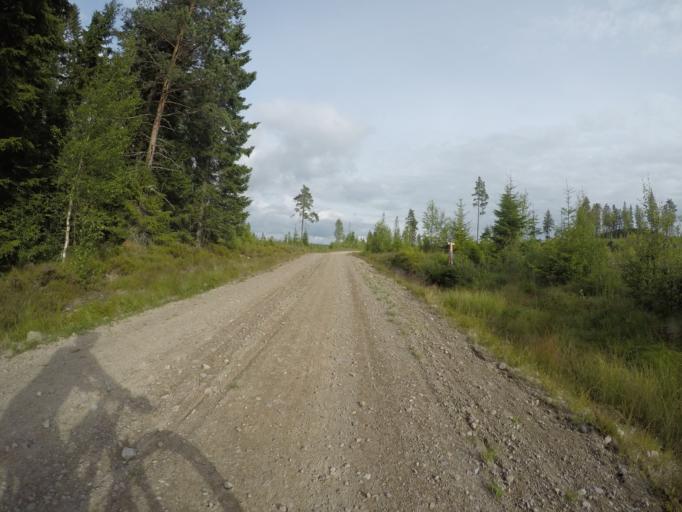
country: SE
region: Vaermland
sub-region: Filipstads Kommun
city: Lesjofors
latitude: 60.2017
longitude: 14.3172
